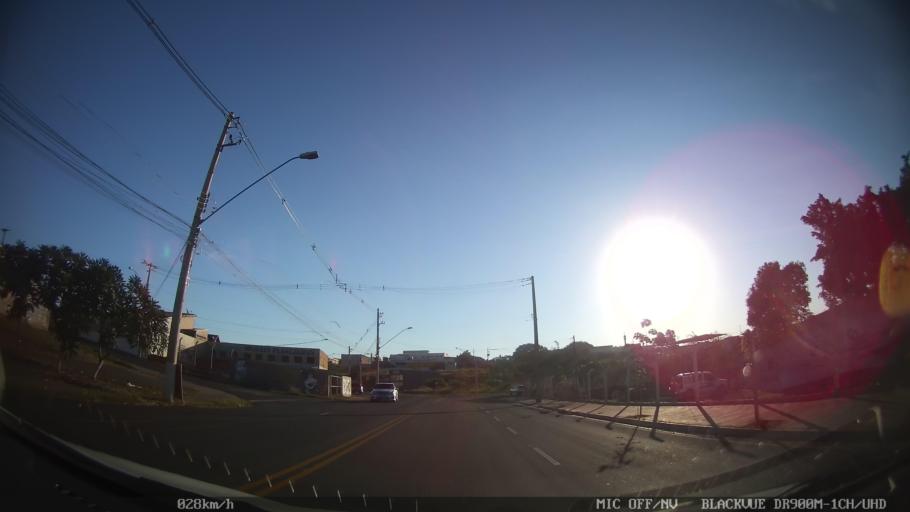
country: BR
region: Sao Paulo
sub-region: Sao Jose Do Rio Preto
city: Sao Jose do Rio Preto
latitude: -20.7917
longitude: -49.3505
